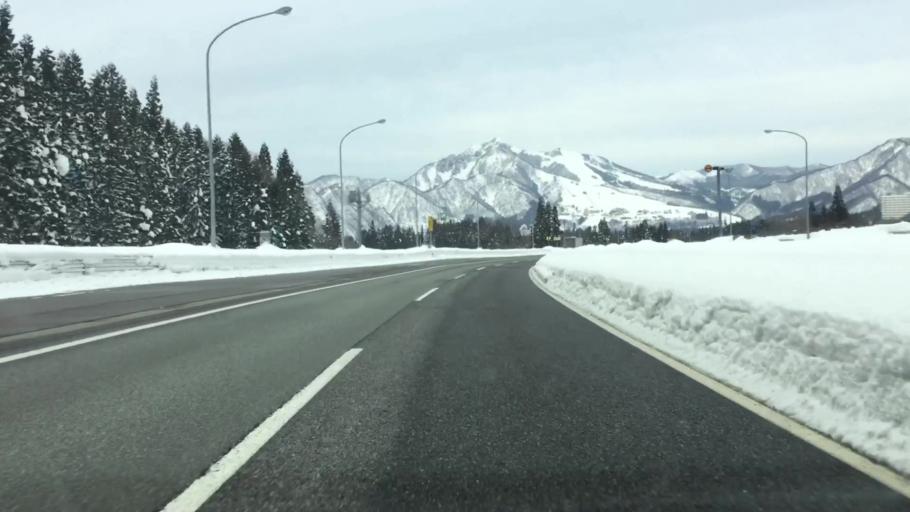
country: JP
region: Niigata
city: Shiozawa
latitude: 36.8945
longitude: 138.8453
